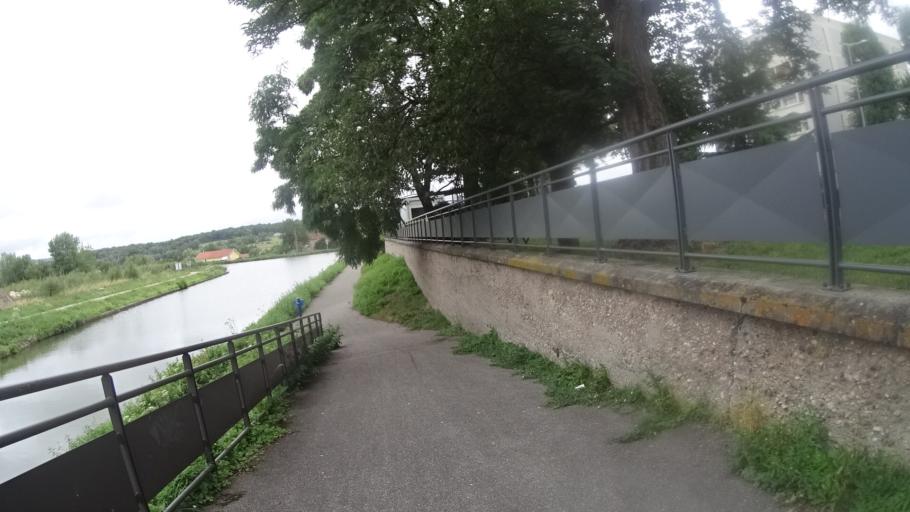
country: FR
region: Lorraine
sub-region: Departement de Meurthe-et-Moselle
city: Laneuveville-devant-Nancy
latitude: 48.6587
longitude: 6.2296
